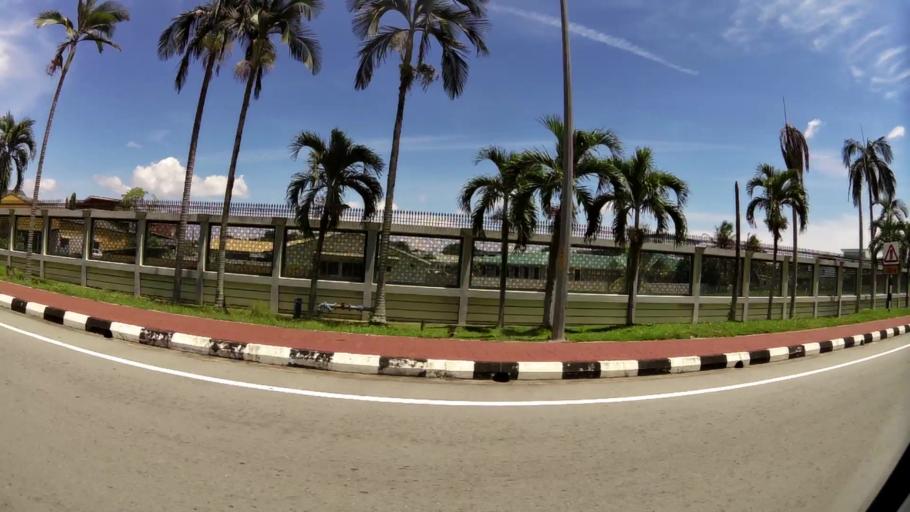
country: BN
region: Brunei and Muara
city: Bandar Seri Begawan
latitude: 4.9319
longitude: 114.9407
